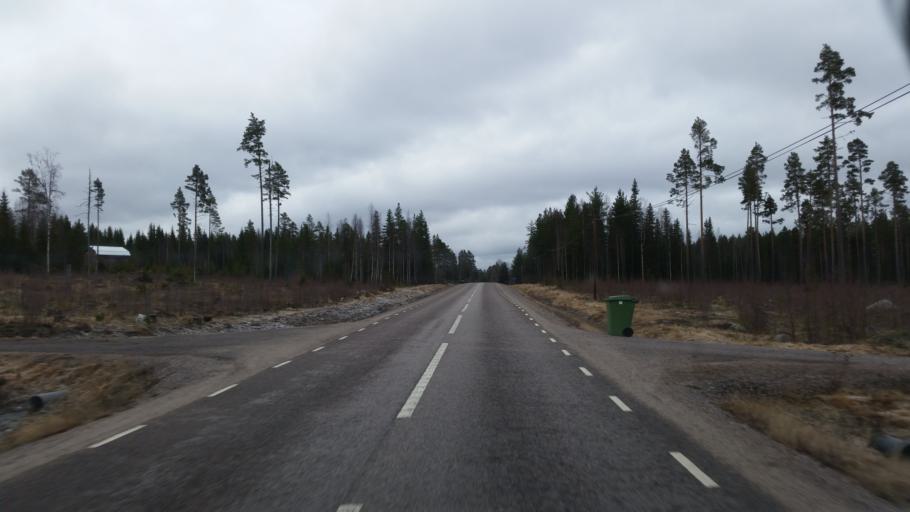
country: SE
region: Gaevleborg
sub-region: Ovanakers Kommun
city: Edsbyn
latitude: 61.4577
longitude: 15.7023
